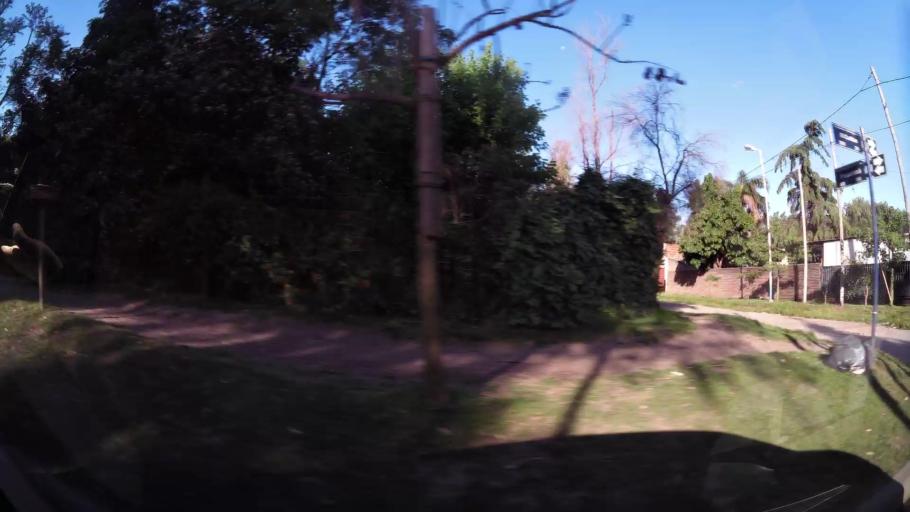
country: AR
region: Buenos Aires
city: Santa Catalina - Dique Lujan
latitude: -34.4665
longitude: -58.7420
